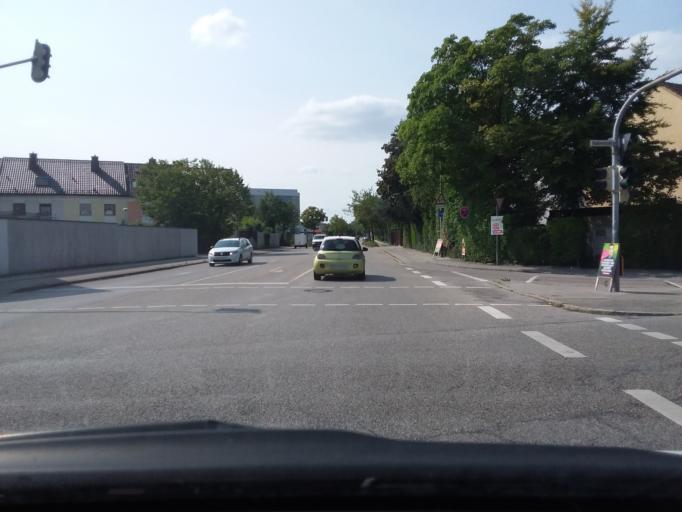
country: DE
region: Bavaria
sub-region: Upper Bavaria
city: Unterschleissheim
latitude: 48.2705
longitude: 11.5852
